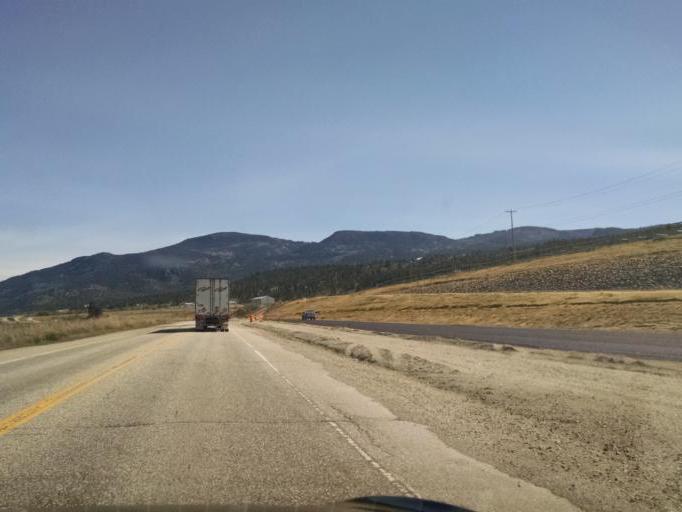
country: CA
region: British Columbia
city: Chase
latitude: 50.6715
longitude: -119.8459
